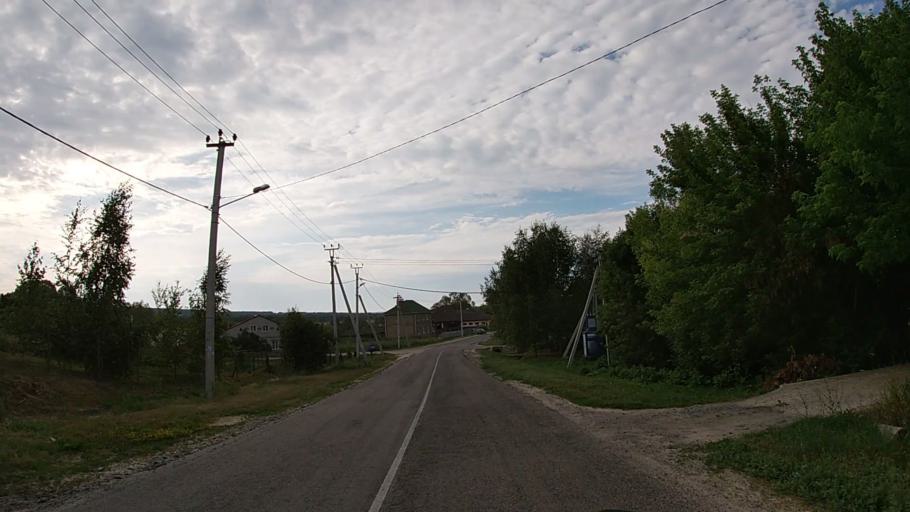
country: RU
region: Belgorod
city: Severnyy
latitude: 50.7123
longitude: 36.5964
